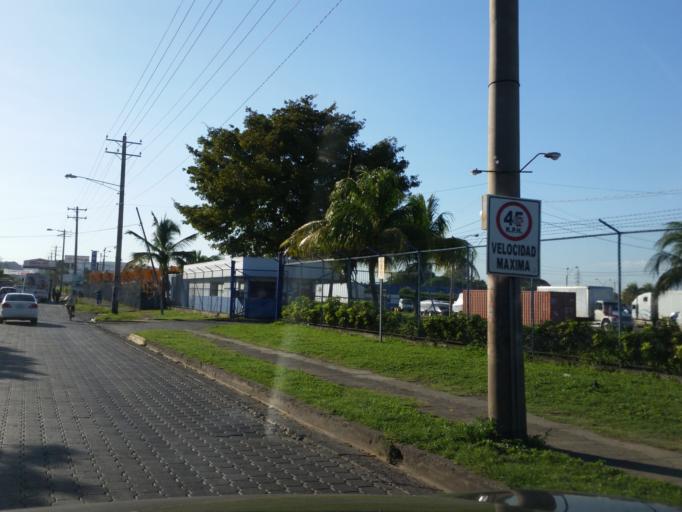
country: NI
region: Managua
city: Ciudad Sandino
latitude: 12.1580
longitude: -86.2983
